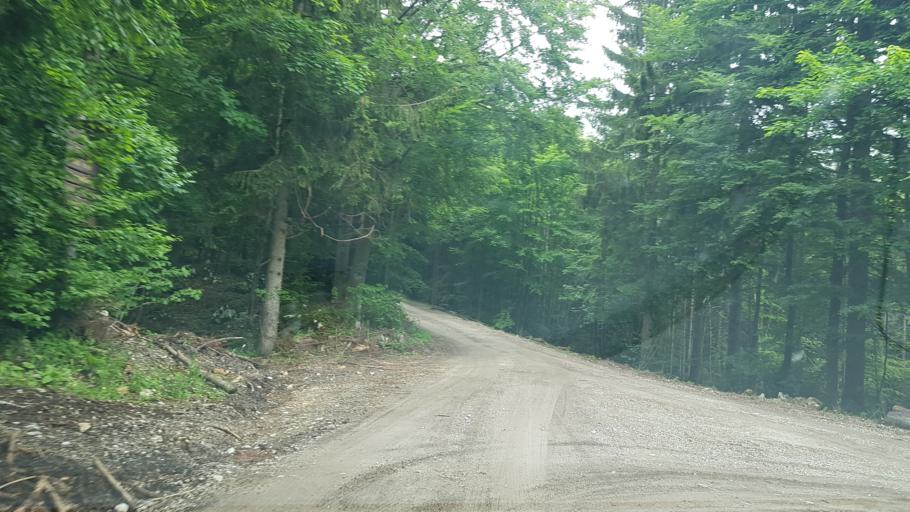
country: SI
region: Dobrna
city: Dobrna
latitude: 46.3779
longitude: 15.2479
